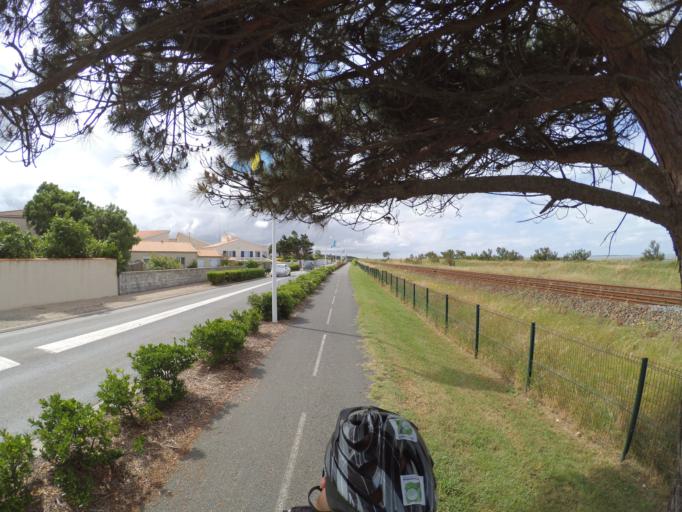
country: FR
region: Poitou-Charentes
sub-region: Departement de la Charente-Maritime
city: Angoulins
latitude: 46.0917
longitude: -1.0993
